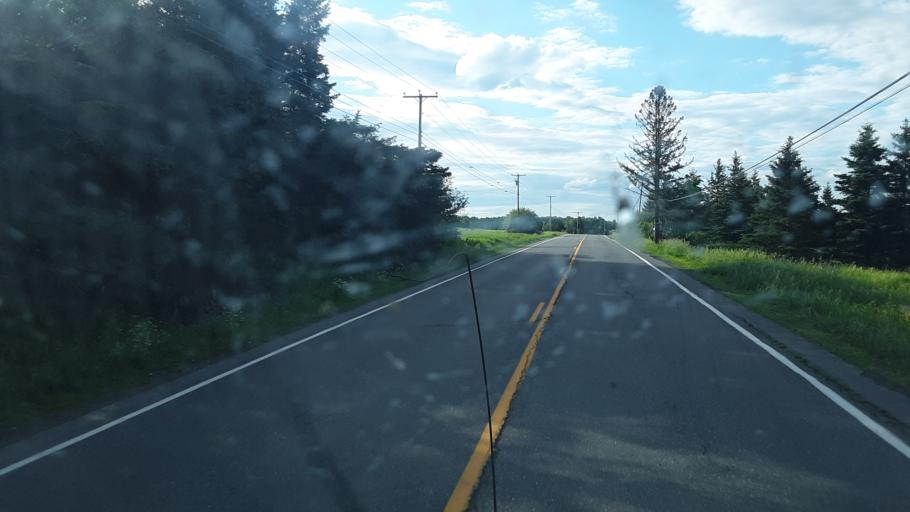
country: US
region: Maine
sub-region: Aroostook County
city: Presque Isle
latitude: 46.6084
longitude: -68.3966
